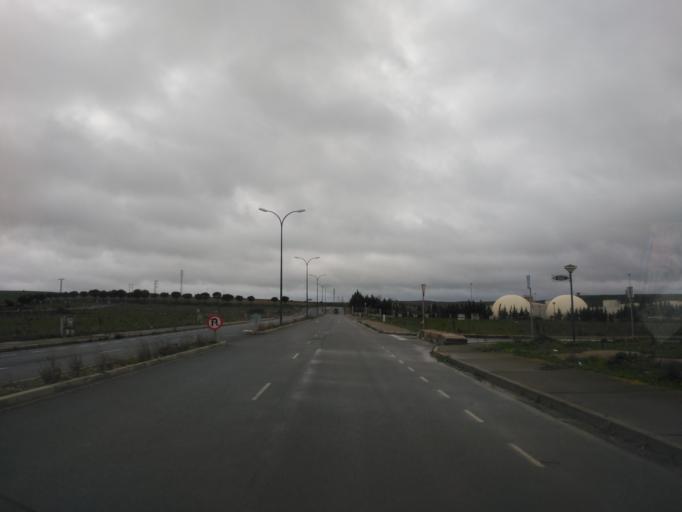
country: ES
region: Castille and Leon
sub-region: Provincia de Salamanca
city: Villamayor
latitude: 40.9760
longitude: -5.7129
